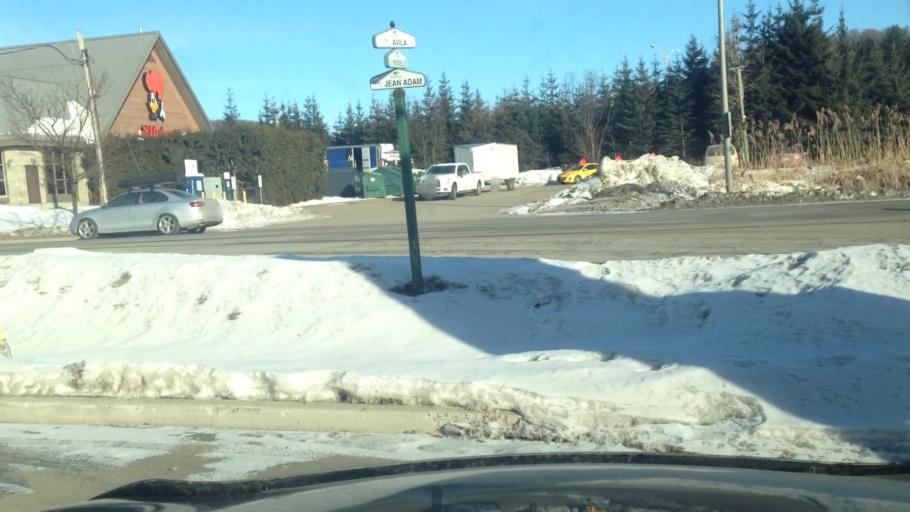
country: CA
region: Quebec
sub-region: Laurentides
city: Saint-Sauveur
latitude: 45.8895
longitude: -74.1456
